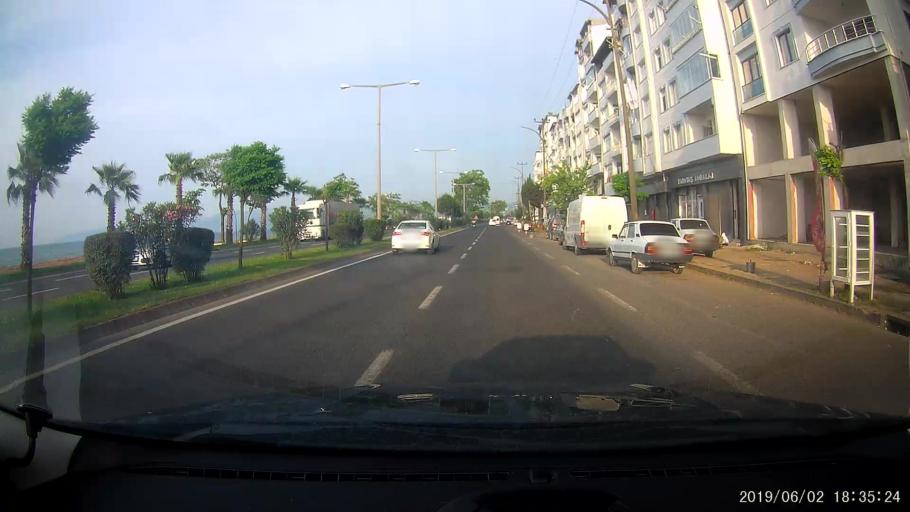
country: TR
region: Ordu
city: Fatsa
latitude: 41.0265
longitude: 37.5156
